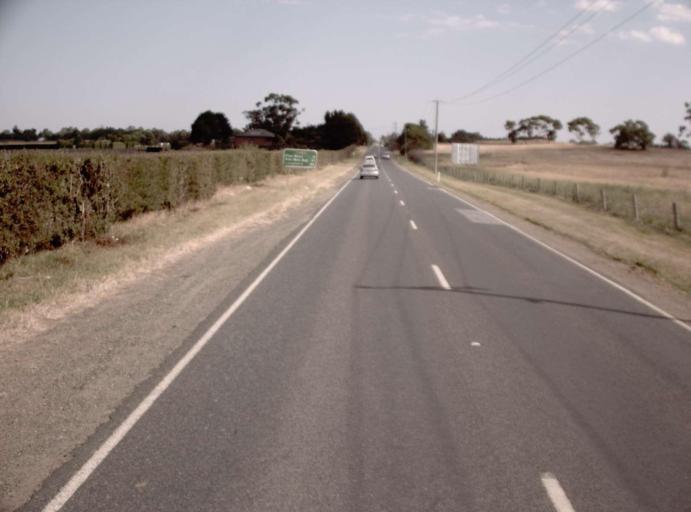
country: AU
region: Victoria
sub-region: Casey
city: Cranbourne East
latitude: -38.1209
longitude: 145.3268
